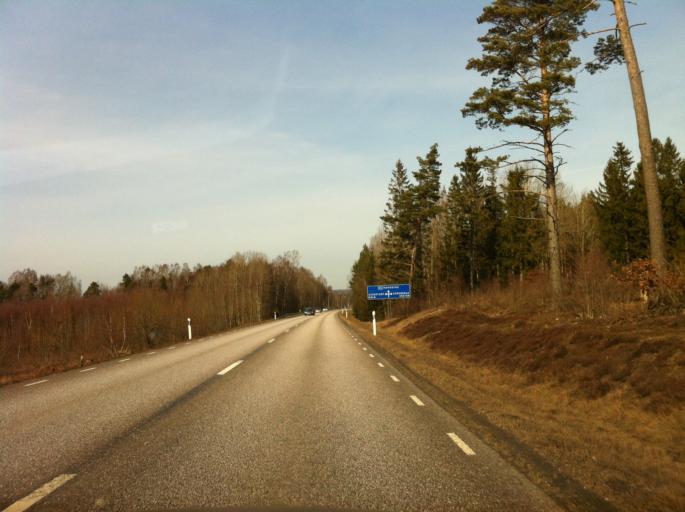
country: SE
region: Vaestra Goetaland
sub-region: Skovde Kommun
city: Skultorp
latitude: 58.2495
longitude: 13.8153
